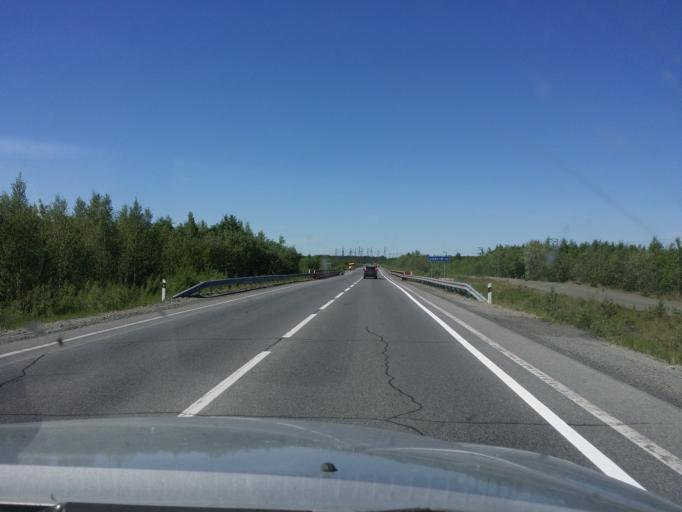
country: RU
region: Khanty-Mansiyskiy Avtonomnyy Okrug
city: Lokosovo
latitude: 61.4866
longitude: 74.1662
